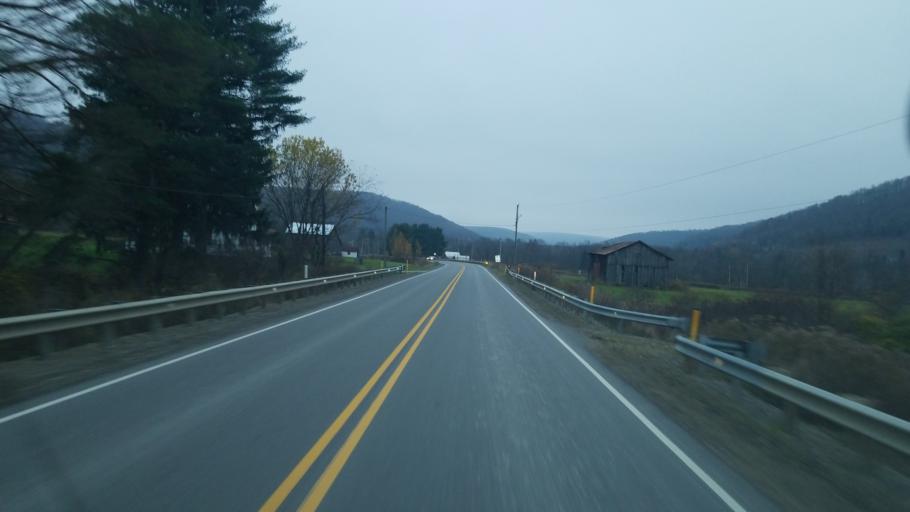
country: US
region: Pennsylvania
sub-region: McKean County
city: Smethport
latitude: 41.7833
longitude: -78.4124
